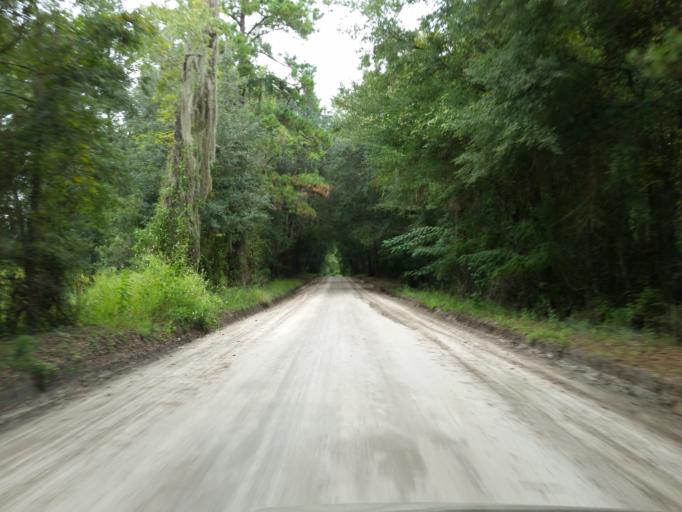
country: US
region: Florida
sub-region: Alachua County
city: High Springs
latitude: 29.9652
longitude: -82.5595
